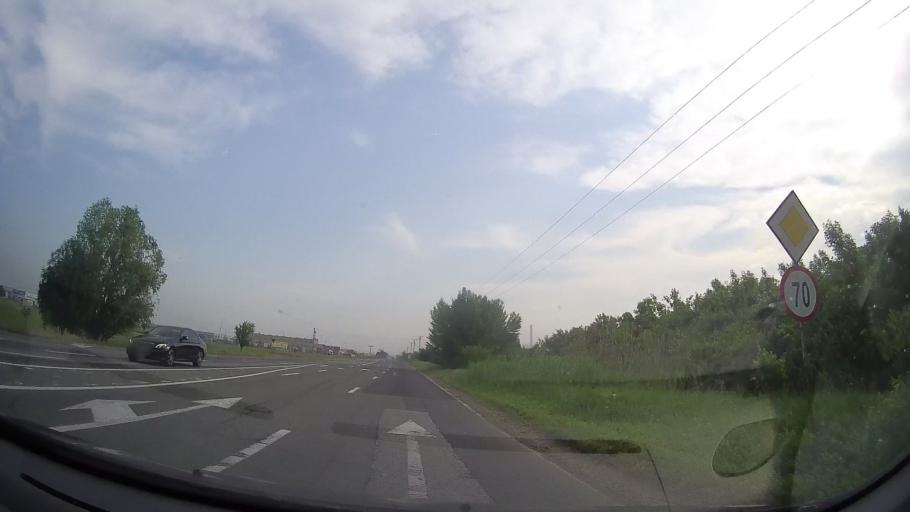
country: RO
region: Timis
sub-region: Comuna Giroc
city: Chisoda
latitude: 45.6923
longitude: 21.1754
